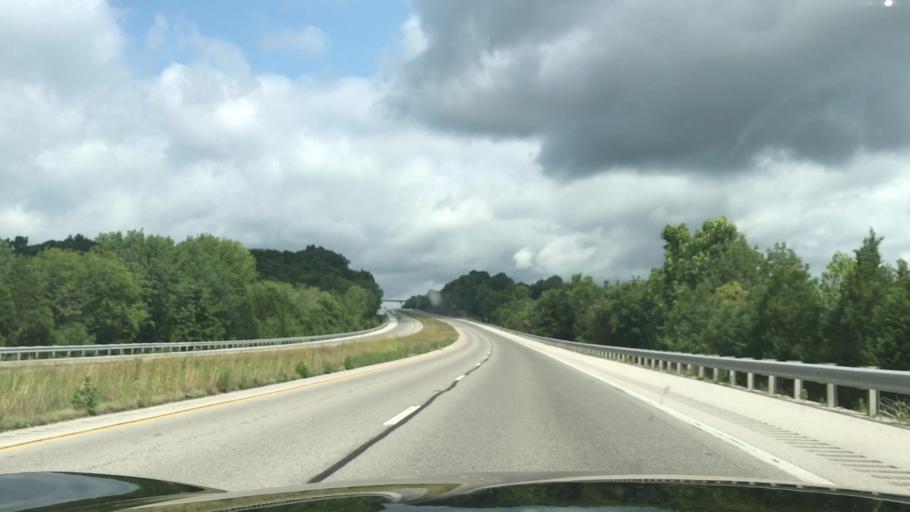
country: US
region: Kentucky
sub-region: Warren County
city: Bowling Green
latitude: 37.0104
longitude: -86.5117
